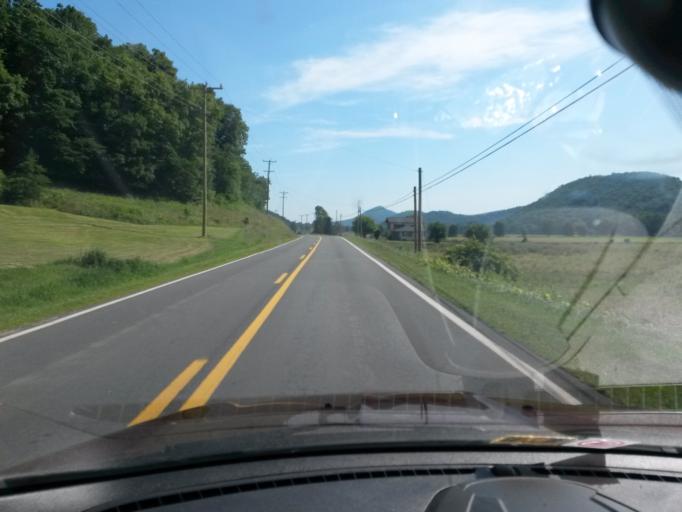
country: US
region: West Virginia
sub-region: Hardy County
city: Moorefield
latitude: 39.0251
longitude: -78.7579
